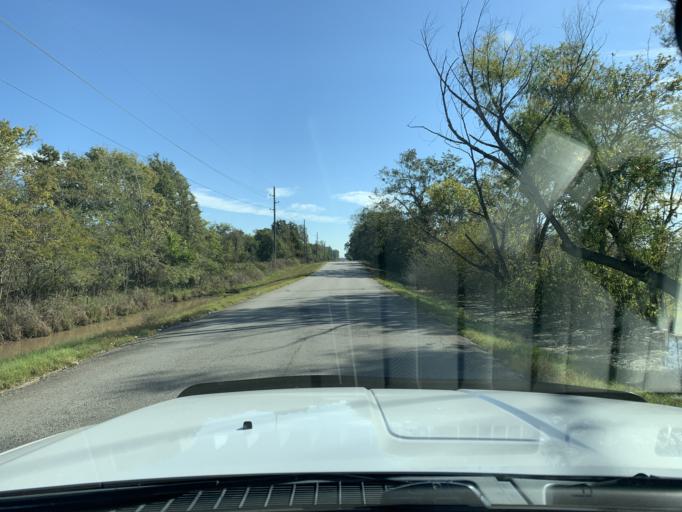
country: US
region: Texas
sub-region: Fort Bend County
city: Rosenberg
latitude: 29.6212
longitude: -95.8319
